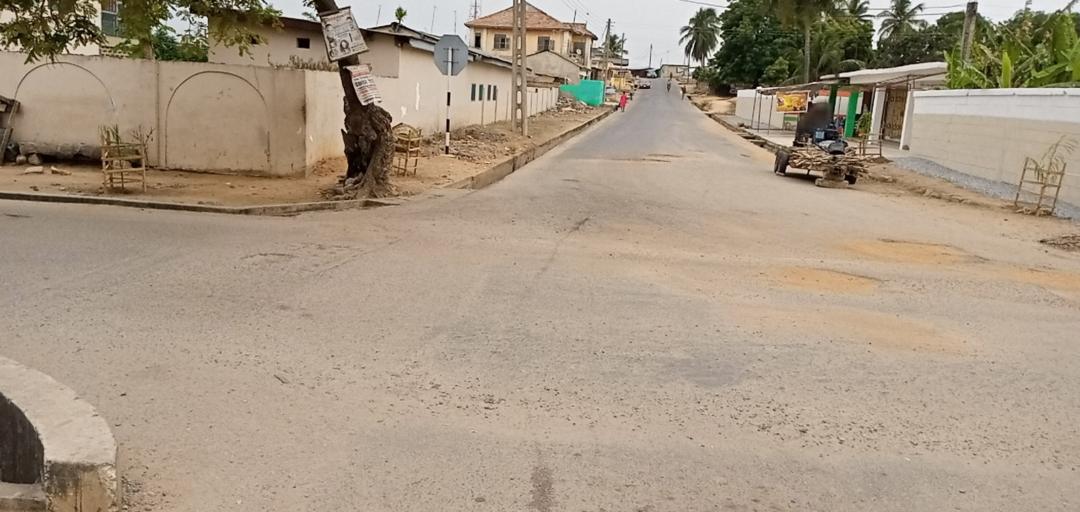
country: GH
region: Central
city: Winneba
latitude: 5.3480
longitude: -0.6257
